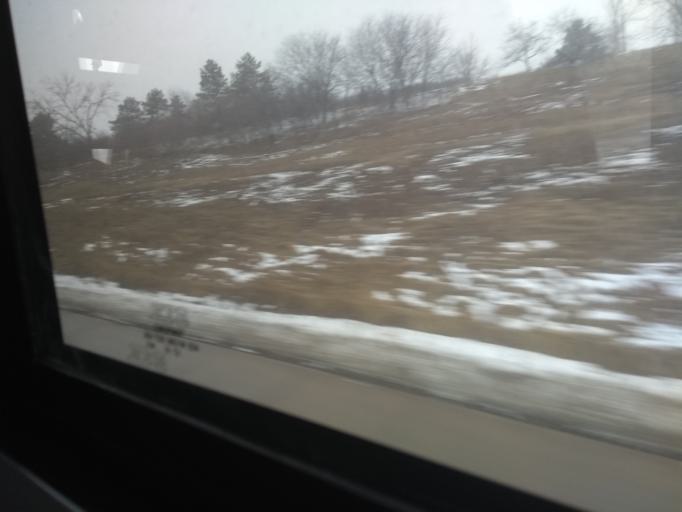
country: CA
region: Ontario
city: Welland
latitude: 42.9936
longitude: -79.2195
